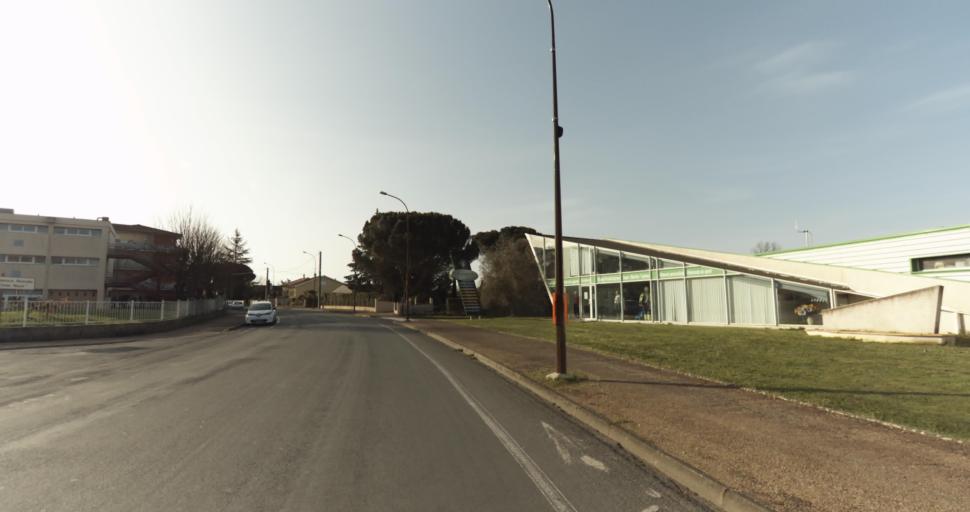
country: FR
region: Midi-Pyrenees
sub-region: Departement du Tarn
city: Saint-Sulpice-la-Pointe
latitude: 43.7718
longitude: 1.6801
